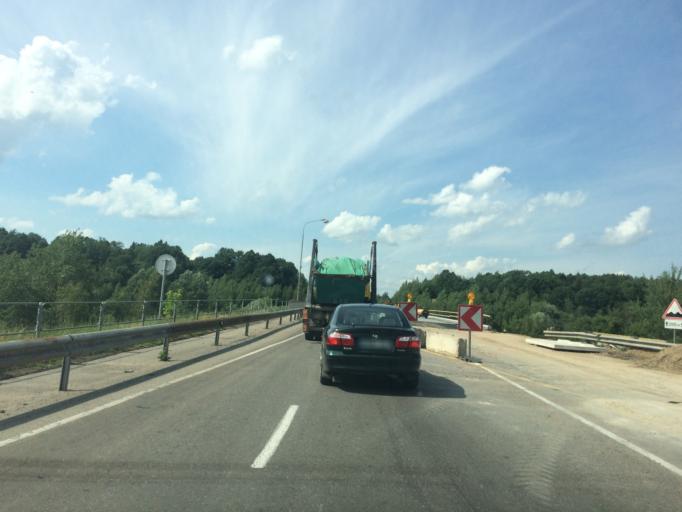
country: LT
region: Kauno apskritis
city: Jonava
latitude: 55.0865
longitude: 24.3162
